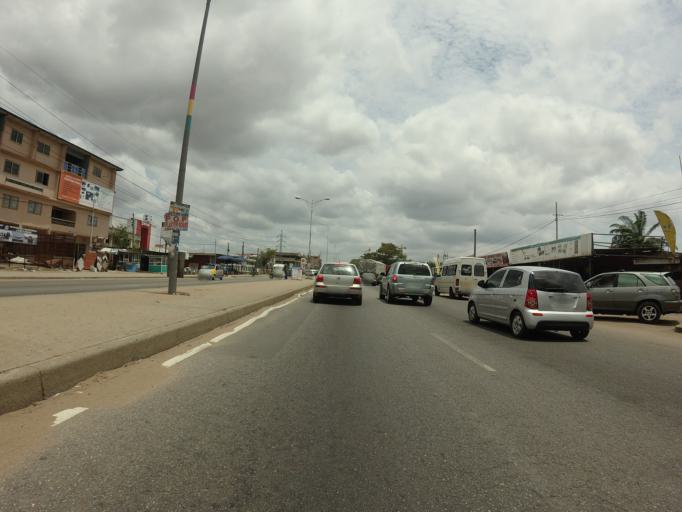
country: GH
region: Greater Accra
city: Gbawe
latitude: 5.5743
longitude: -0.2778
